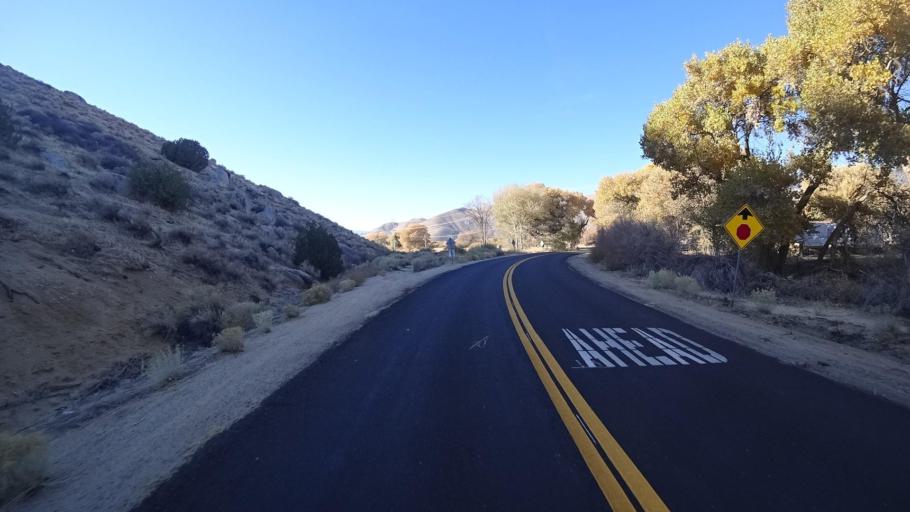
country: US
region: California
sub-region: Kern County
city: Weldon
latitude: 35.6634
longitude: -118.3026
